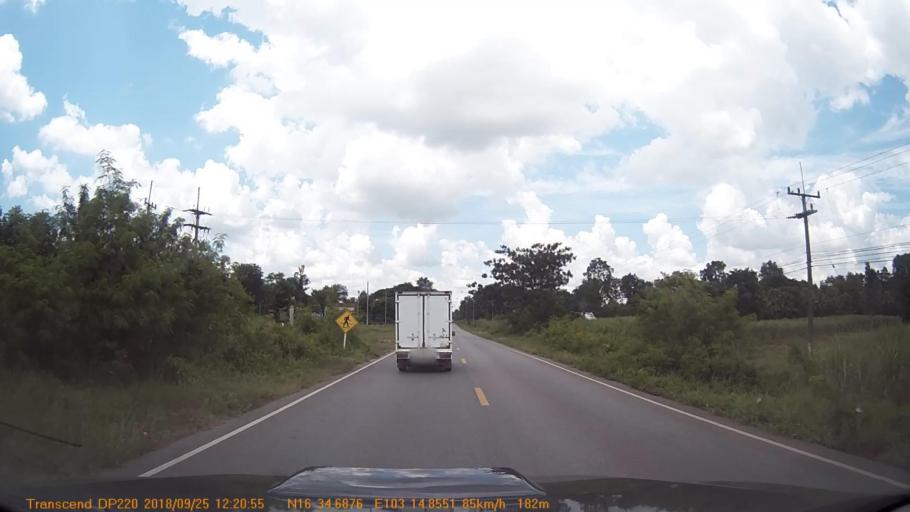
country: TH
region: Kalasin
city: Huai Mek
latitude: 16.5782
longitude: 103.2475
